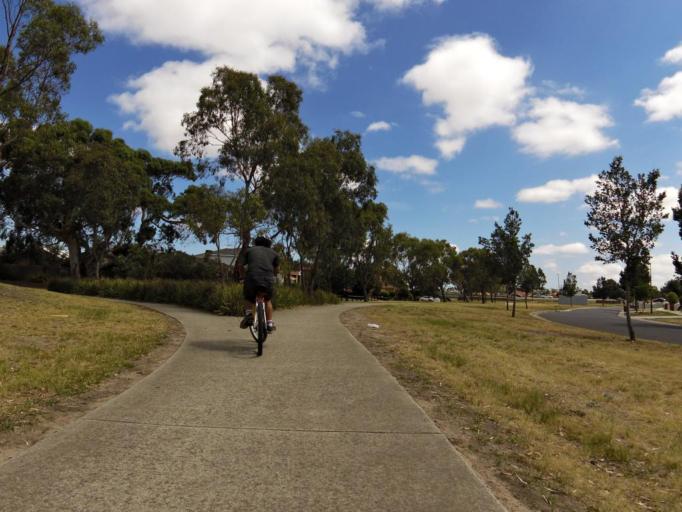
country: AU
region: Victoria
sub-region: Hume
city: Roxburgh Park
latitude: -37.6178
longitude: 144.9297
